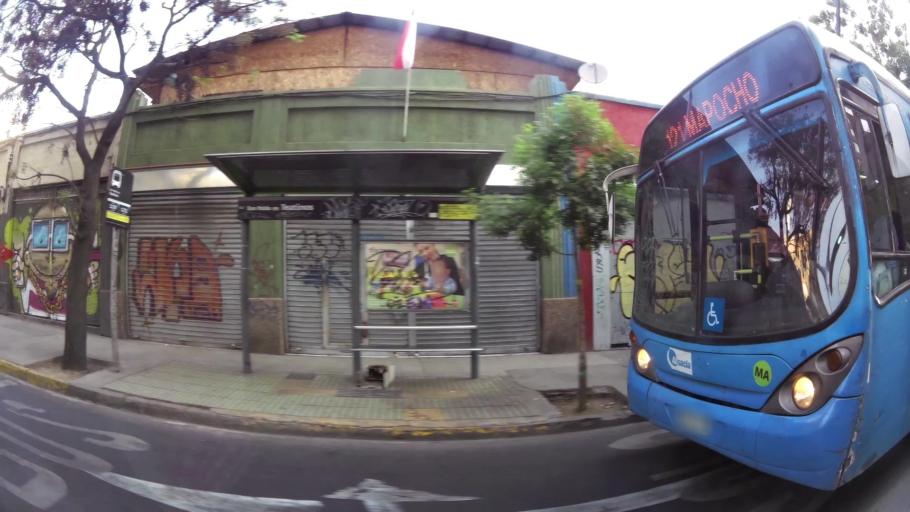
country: CL
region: Santiago Metropolitan
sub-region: Provincia de Santiago
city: Santiago
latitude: -33.4344
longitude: -70.6562
